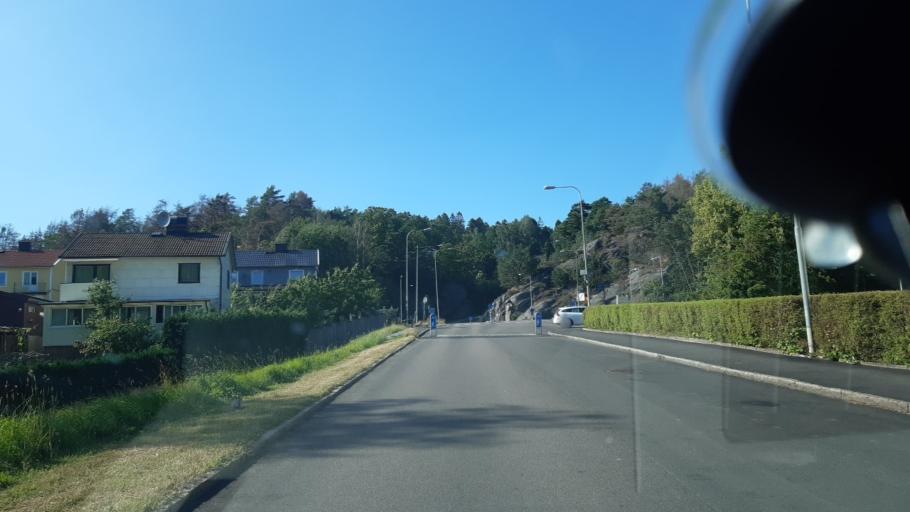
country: SE
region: Vaestra Goetaland
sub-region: Goteborg
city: Eriksbo
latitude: 57.7711
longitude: 12.0336
